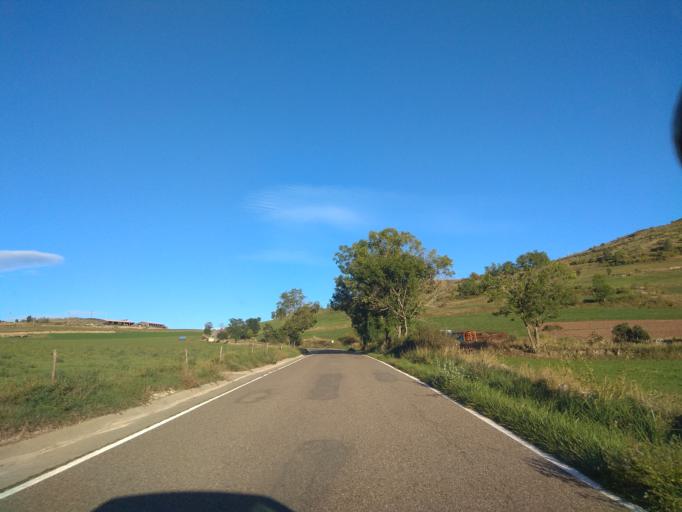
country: ES
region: Catalonia
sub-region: Provincia de Lleida
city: Lles de Cerdanya
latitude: 42.3507
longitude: 1.6935
